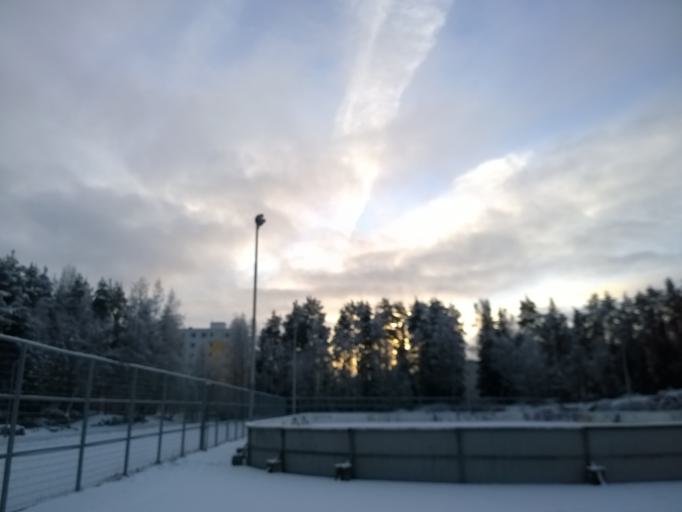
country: FI
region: Pirkanmaa
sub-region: Tampere
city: Tampere
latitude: 61.4469
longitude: 23.8427
